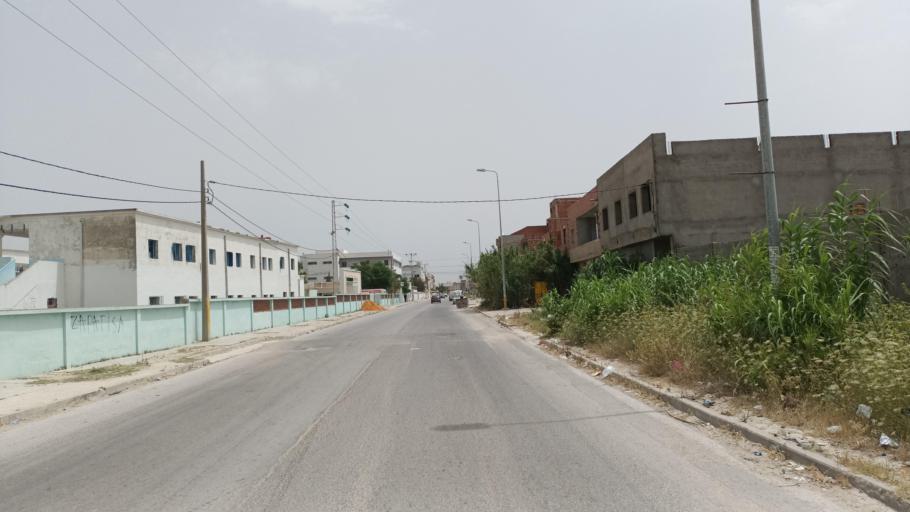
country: TN
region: Nabul
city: Manzil Bu Zalafah
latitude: 36.7080
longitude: 10.4844
